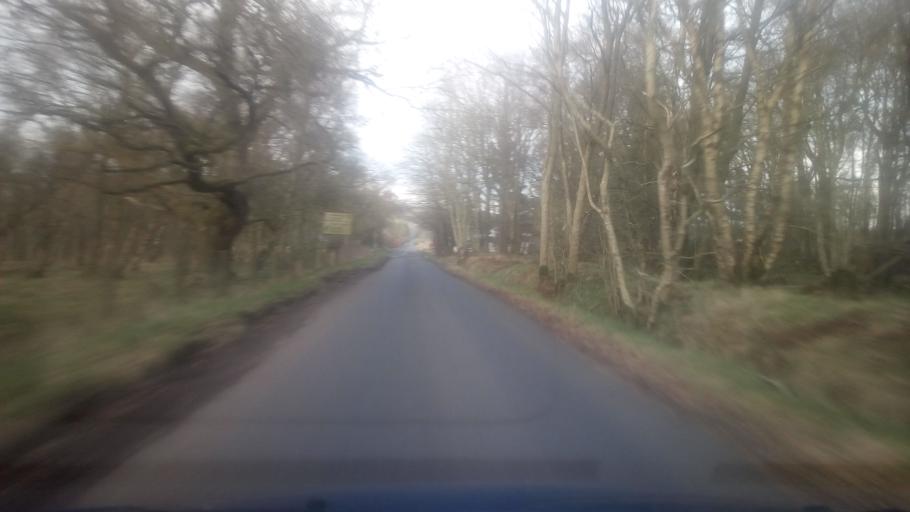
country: GB
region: Scotland
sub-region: The Scottish Borders
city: Jedburgh
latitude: 55.4217
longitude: -2.6180
